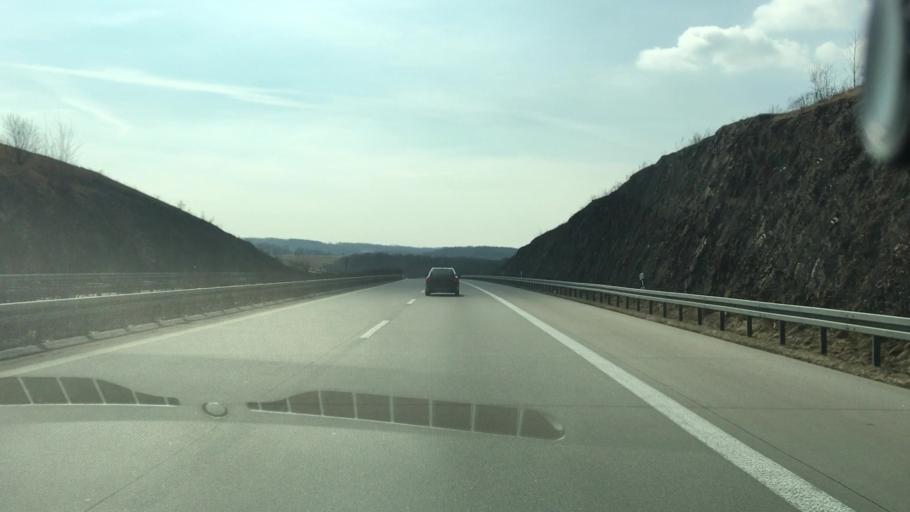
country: DE
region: Saxony
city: Liebstadt
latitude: 50.8760
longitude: 13.8720
